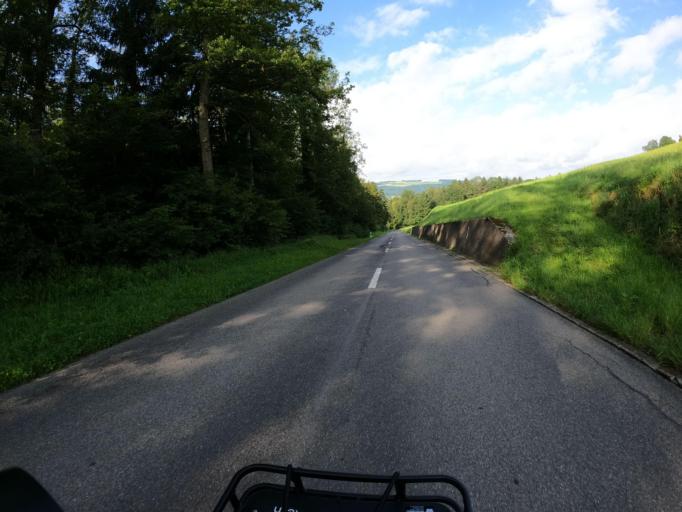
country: CH
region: Lucerne
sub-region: Hochdorf District
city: Hitzkirch
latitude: 47.2170
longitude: 8.2798
